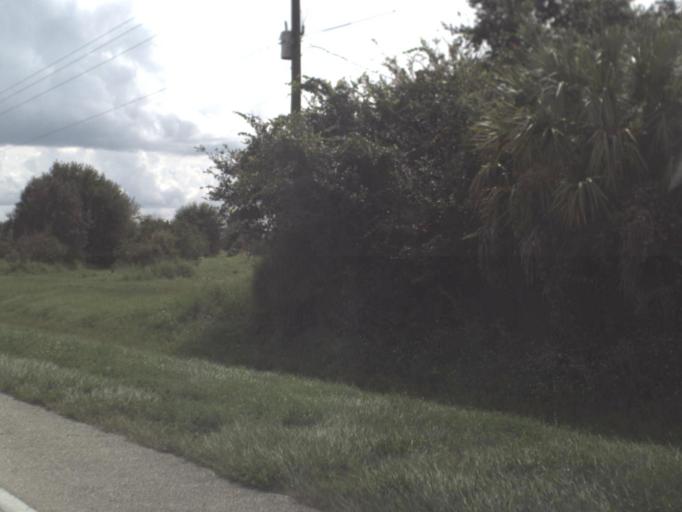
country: US
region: Florida
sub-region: DeSoto County
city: Nocatee
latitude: 27.0671
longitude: -81.7934
